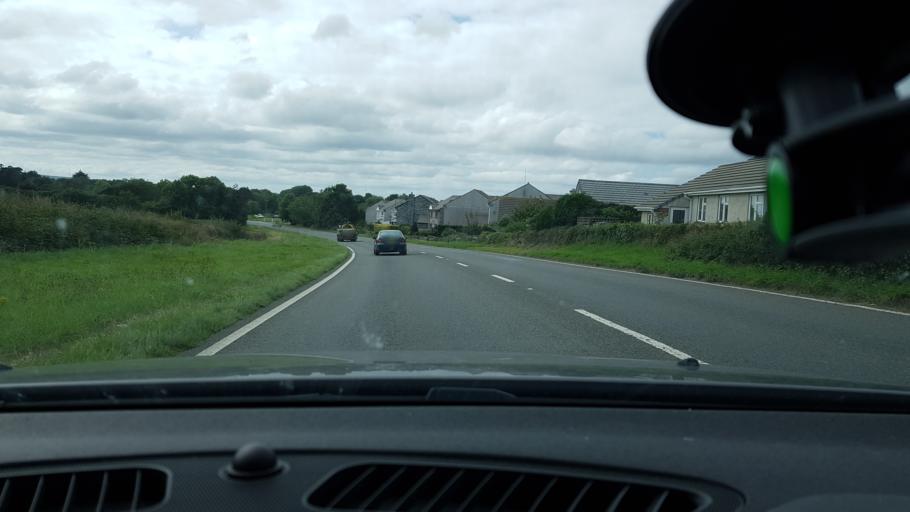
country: GB
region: England
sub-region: Cornwall
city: Wadebridge
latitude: 50.5470
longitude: -4.7744
